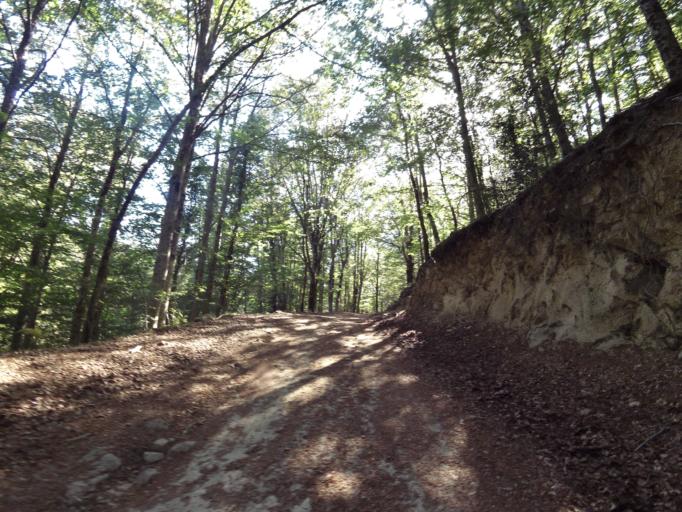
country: IT
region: Calabria
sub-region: Provincia di Vibo-Valentia
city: Nardodipace
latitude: 38.5128
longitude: 16.3756
